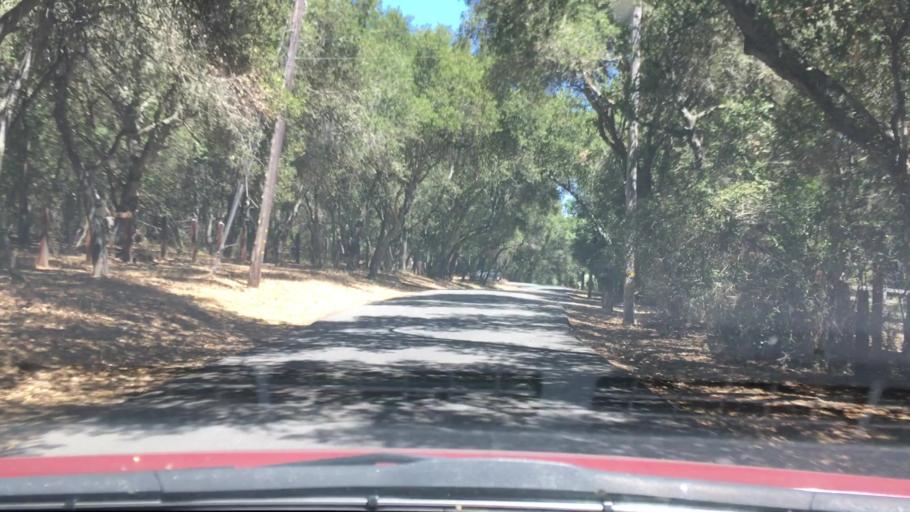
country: US
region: California
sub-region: San Mateo County
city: Woodside
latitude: 37.4316
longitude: -122.2659
